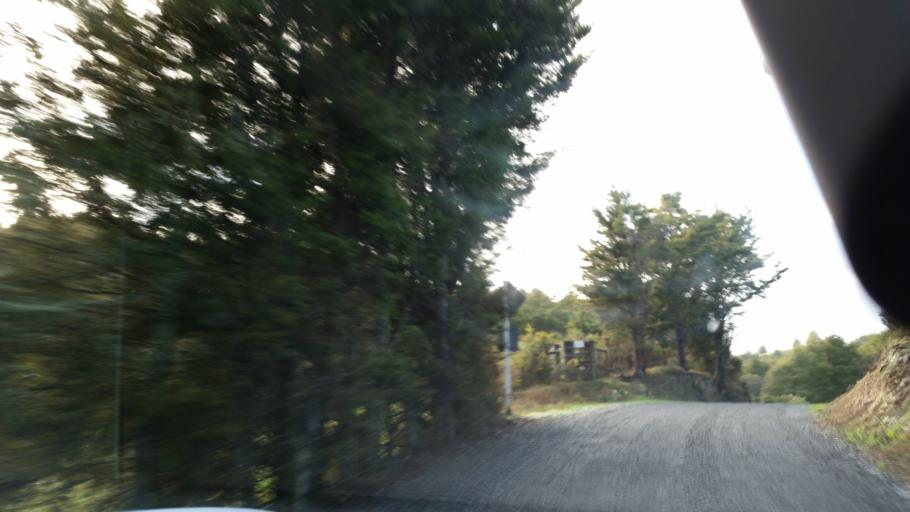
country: NZ
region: Northland
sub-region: Whangarei
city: Maungatapere
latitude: -35.7785
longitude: 174.0895
